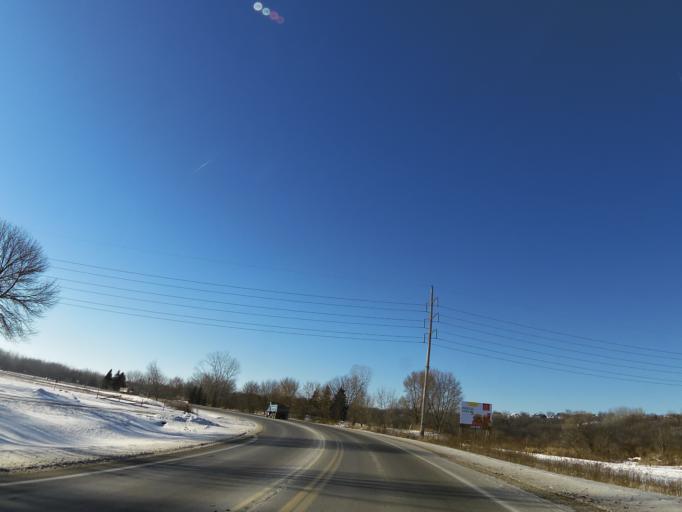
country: US
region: Minnesota
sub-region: Carver County
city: Chaska
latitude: 44.8074
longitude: -93.5703
